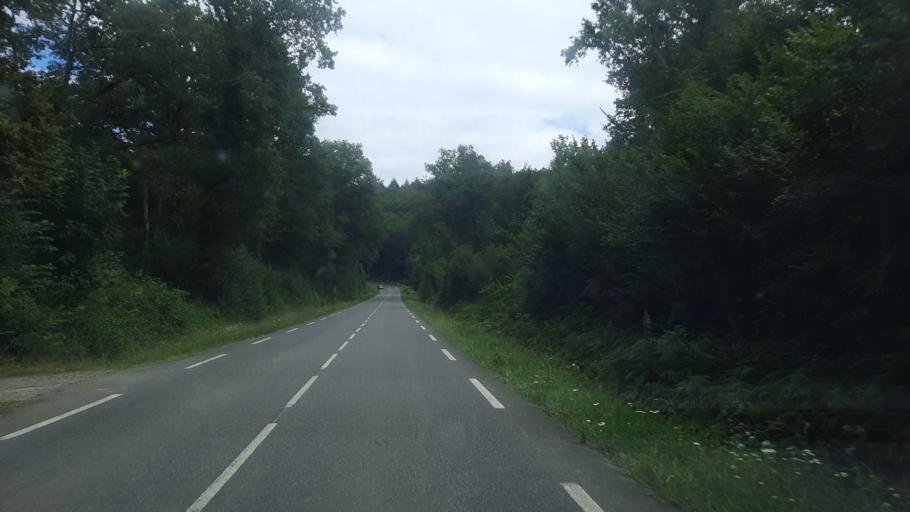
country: FR
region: Midi-Pyrenees
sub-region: Departement des Hautes-Pyrenees
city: Trie-sur-Baise
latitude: 43.2986
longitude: 0.4294
